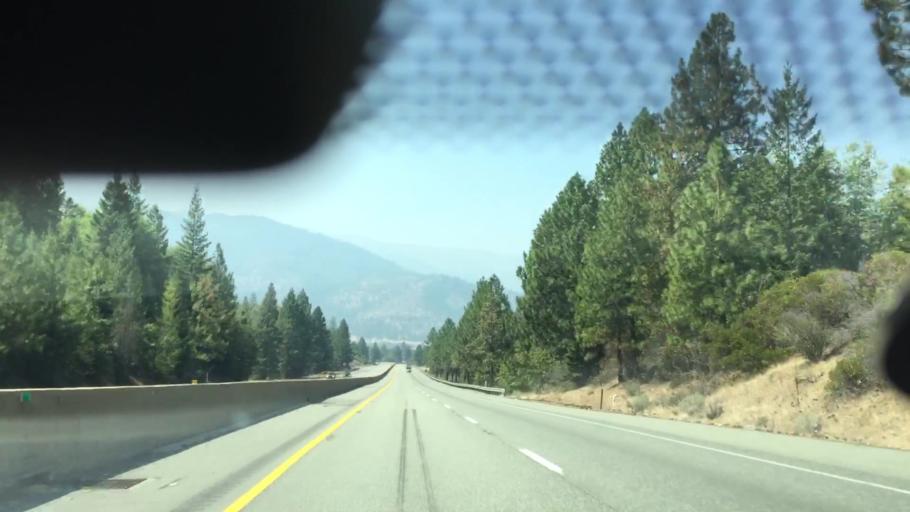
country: US
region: California
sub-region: Siskiyou County
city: Weed
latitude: 41.4306
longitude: -122.4102
